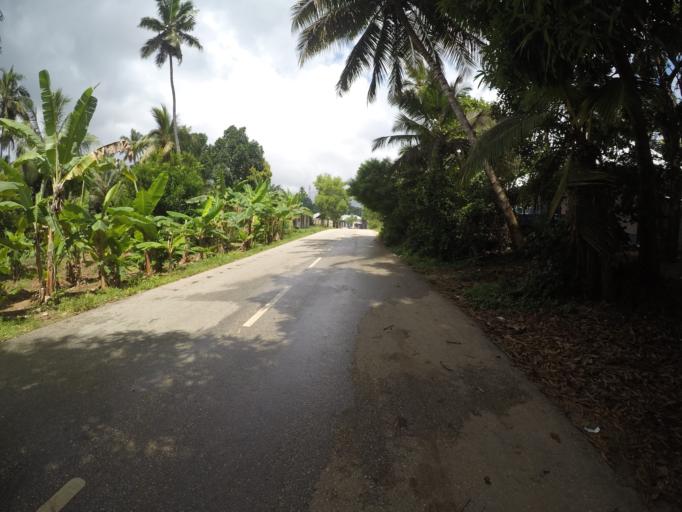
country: TZ
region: Pemba South
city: Mtambile
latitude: -5.3855
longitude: 39.7447
